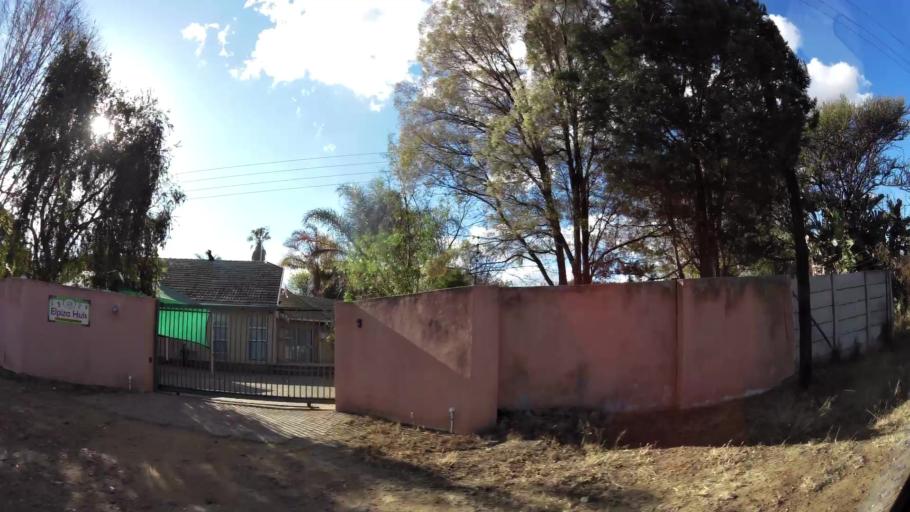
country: ZA
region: Limpopo
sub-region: Capricorn District Municipality
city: Polokwane
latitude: -23.9299
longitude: 29.4463
